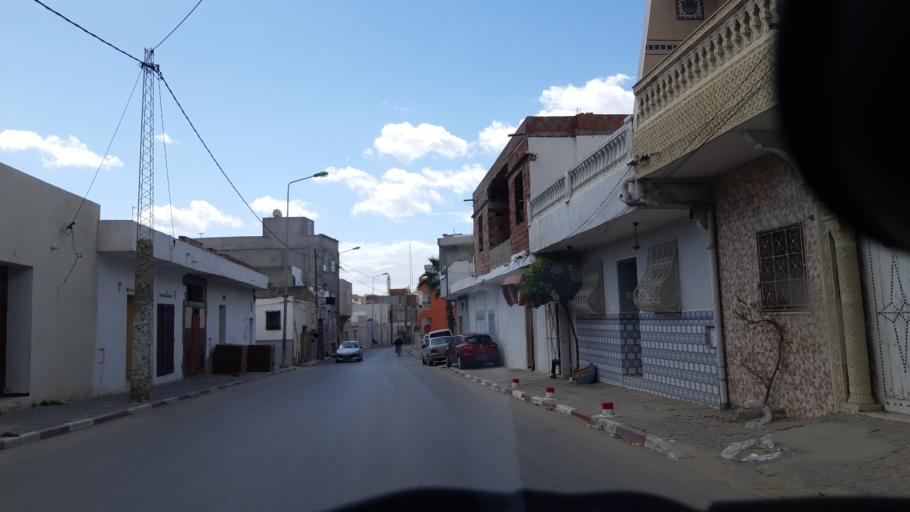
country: TN
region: Susah
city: Akouda
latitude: 35.8785
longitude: 10.5369
